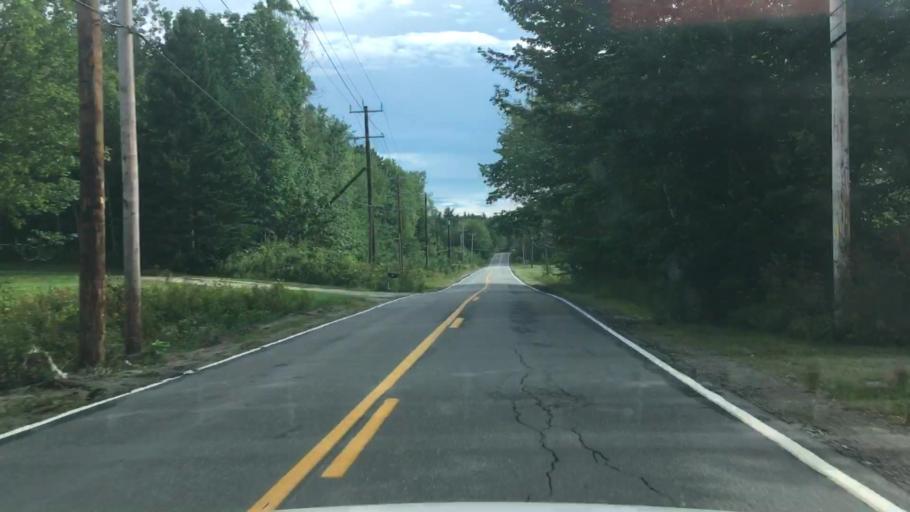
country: US
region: Maine
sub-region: Hancock County
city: Ellsworth
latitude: 44.4869
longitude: -68.4201
